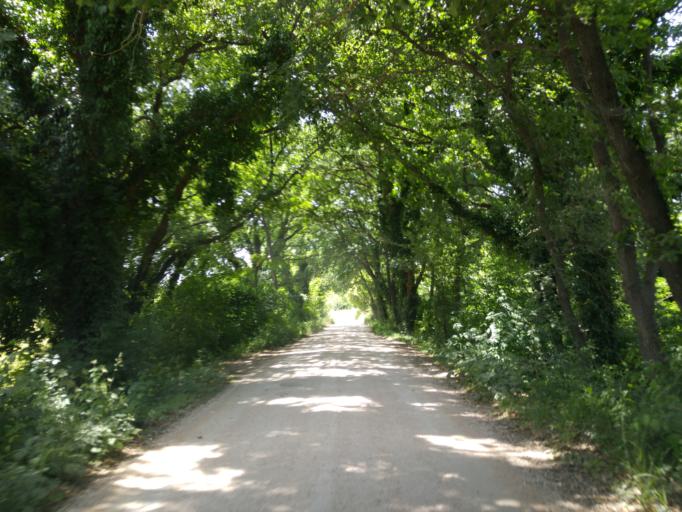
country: IT
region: The Marches
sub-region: Provincia di Pesaro e Urbino
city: Bellocchi
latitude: 43.7779
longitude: 12.9962
